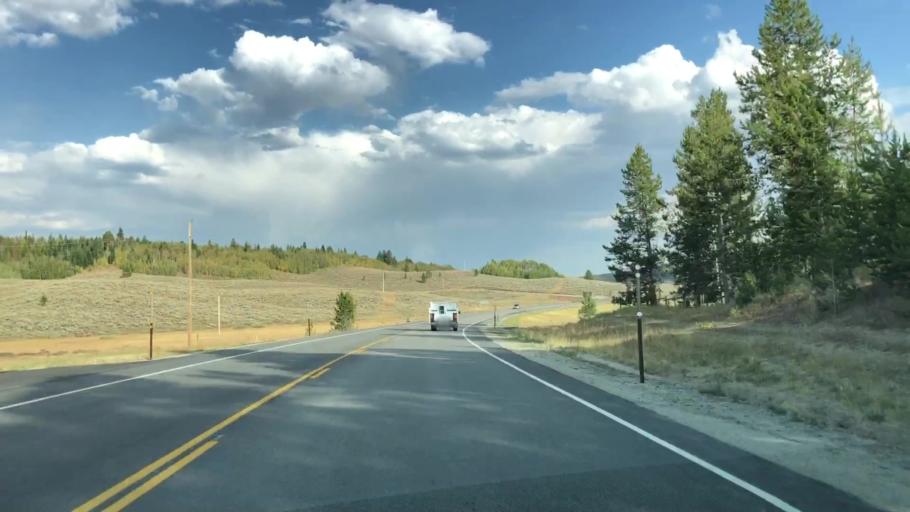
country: US
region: Wyoming
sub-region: Sublette County
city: Pinedale
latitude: 43.1323
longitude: -110.1959
